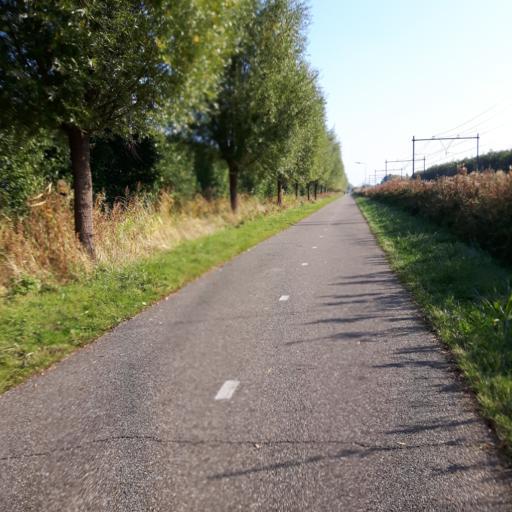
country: NL
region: Zeeland
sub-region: Gemeente Goes
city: Goes
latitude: 51.4881
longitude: 3.9350
